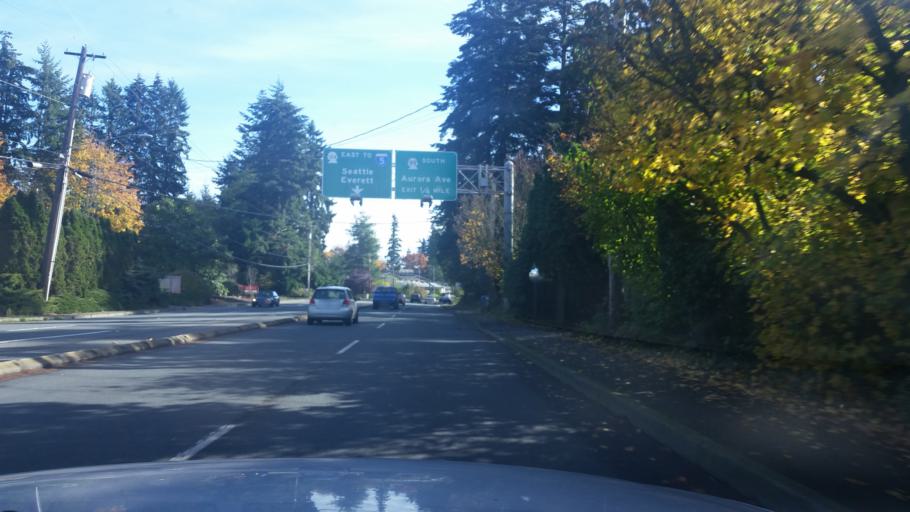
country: US
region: Washington
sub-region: Snohomish County
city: Esperance
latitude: 47.7831
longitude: -122.3514
